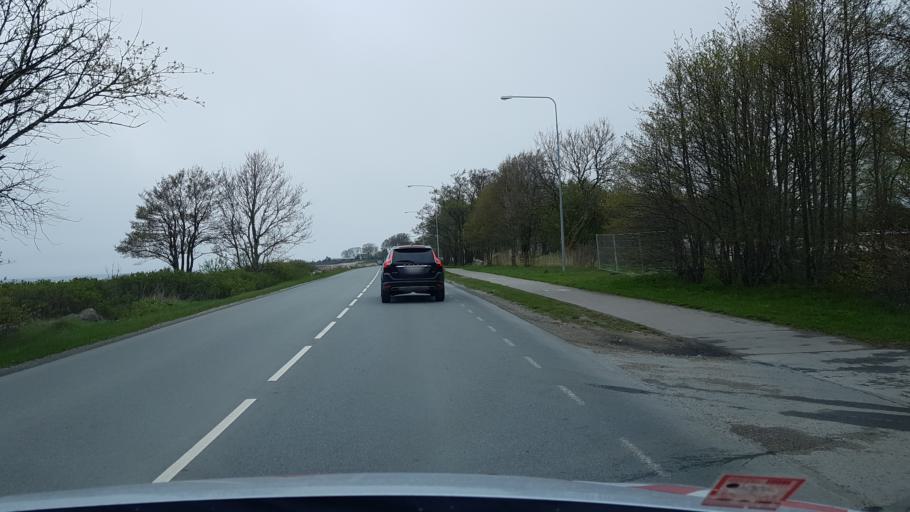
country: EE
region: Harju
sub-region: Viimsi vald
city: Rummu
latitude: 59.5345
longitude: 24.7931
